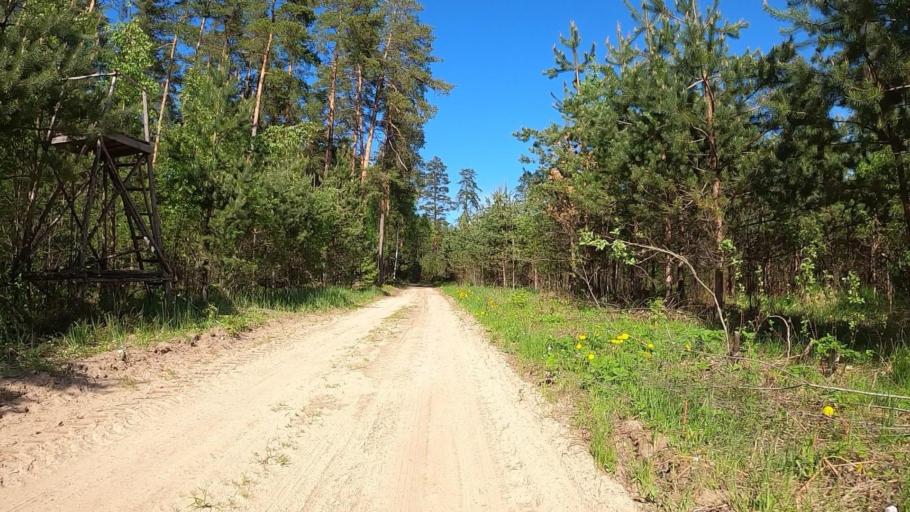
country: LV
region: Salaspils
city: Salaspils
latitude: 56.7893
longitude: 24.3277
